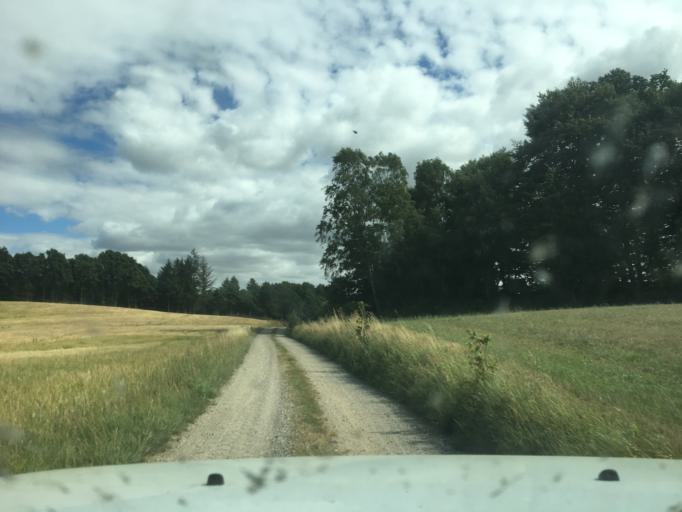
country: DK
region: Central Jutland
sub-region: Syddjurs Kommune
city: Ryomgard
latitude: 56.4847
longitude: 10.6135
